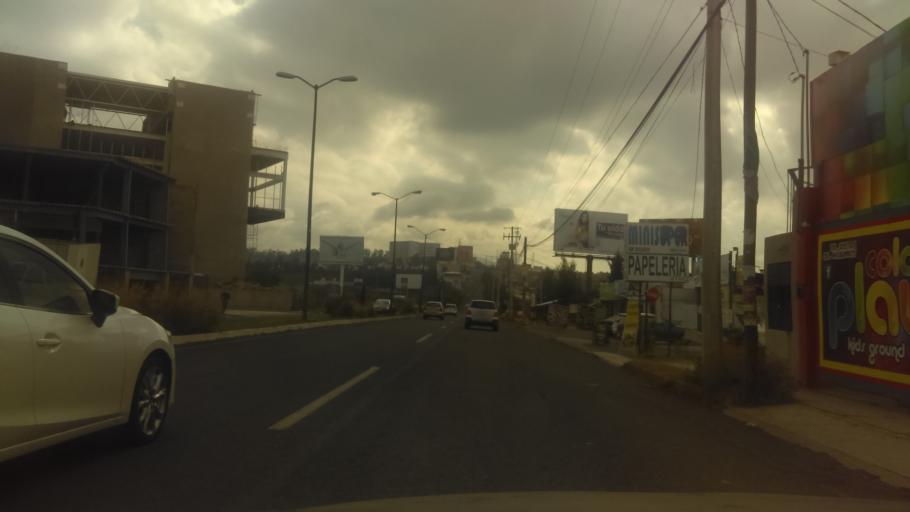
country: MX
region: Michoacan
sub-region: Morelia
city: Montana Monarca (Punta Altozano)
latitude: 19.6729
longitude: -101.1750
